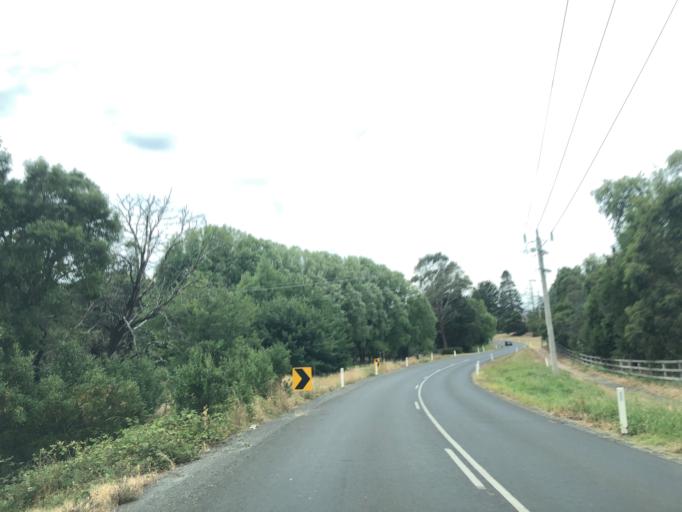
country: AU
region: Victoria
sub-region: Hume
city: Sunbury
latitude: -37.3621
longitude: 144.5207
